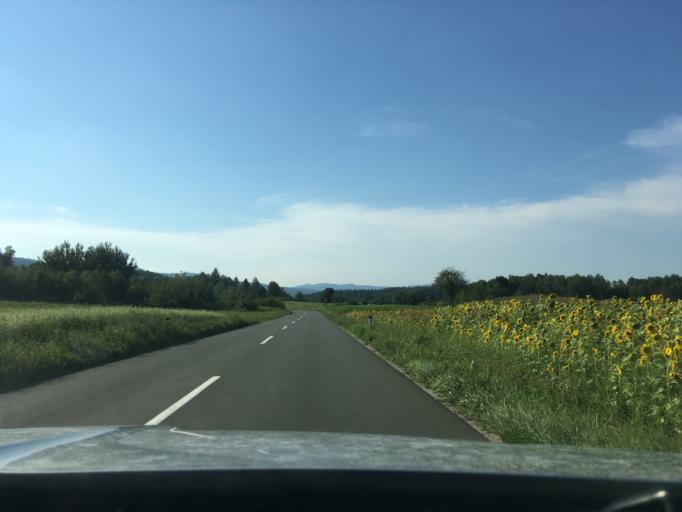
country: SI
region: Crnomelj
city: Crnomelj
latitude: 45.4859
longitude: 15.1956
